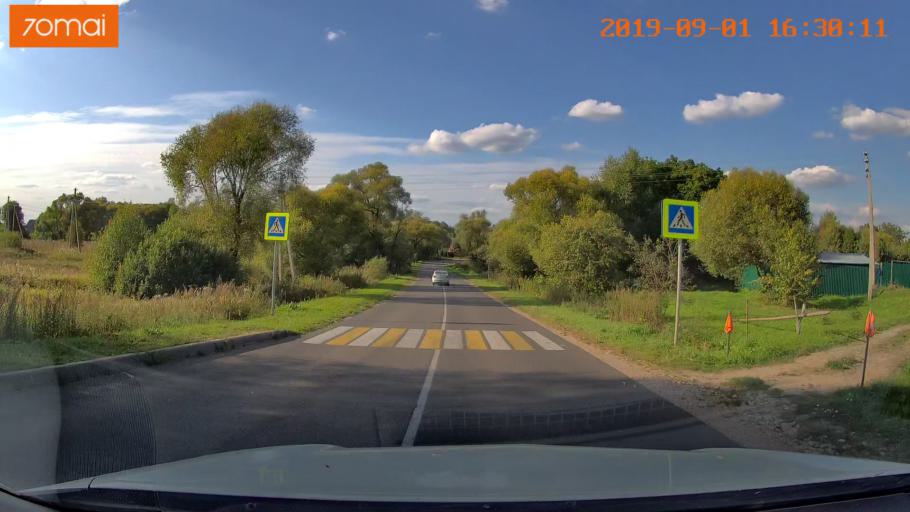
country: RU
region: Kaluga
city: Maloyaroslavets
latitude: 54.9425
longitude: 36.4590
